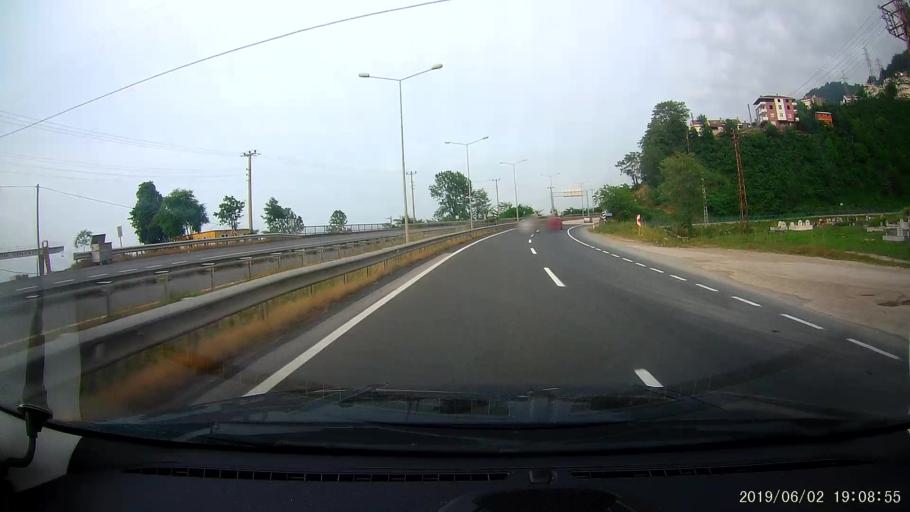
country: TR
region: Ordu
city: Gulyali
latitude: 40.9763
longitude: 38.0190
